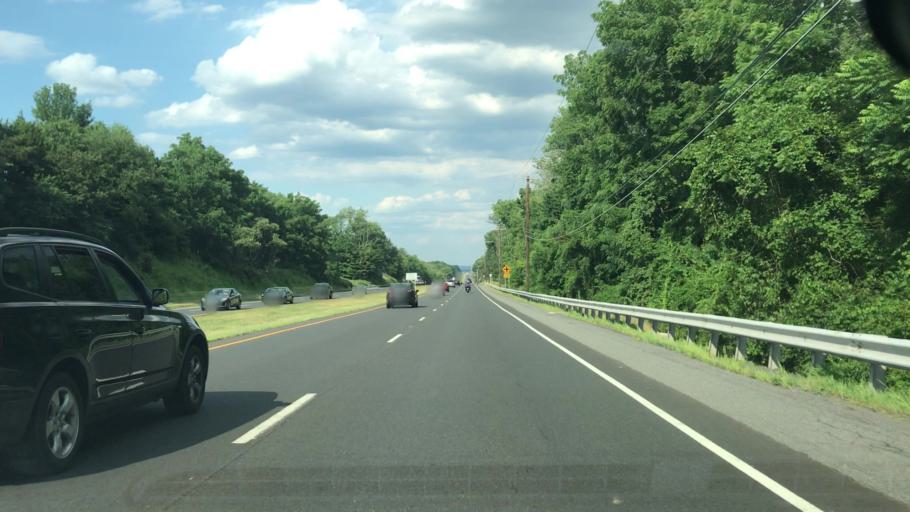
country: US
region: New Jersey
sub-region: Hunterdon County
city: Whitehouse Station
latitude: 40.5503
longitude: -74.7321
